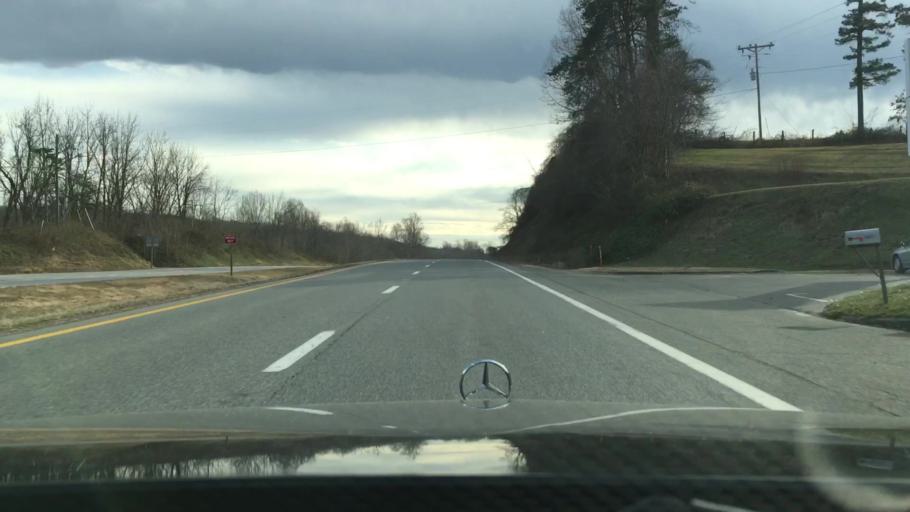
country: US
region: Virginia
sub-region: Pittsylvania County
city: Motley
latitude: 37.0241
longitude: -79.3583
